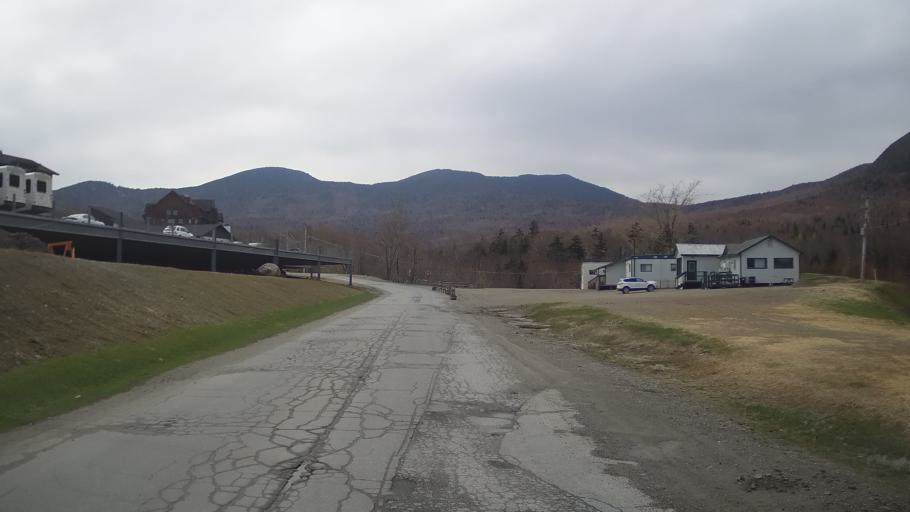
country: US
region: Vermont
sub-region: Franklin County
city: Richford
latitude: 44.9386
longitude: -72.5025
